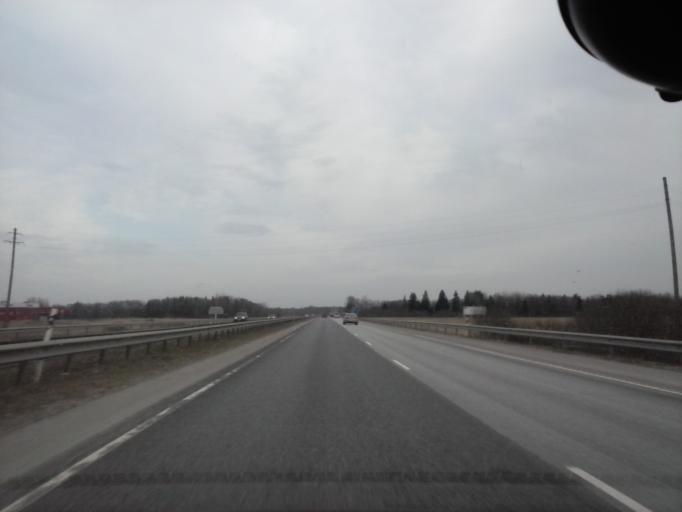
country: EE
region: Harju
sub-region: Rae vald
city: Jueri
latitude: 59.3455
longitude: 24.8943
